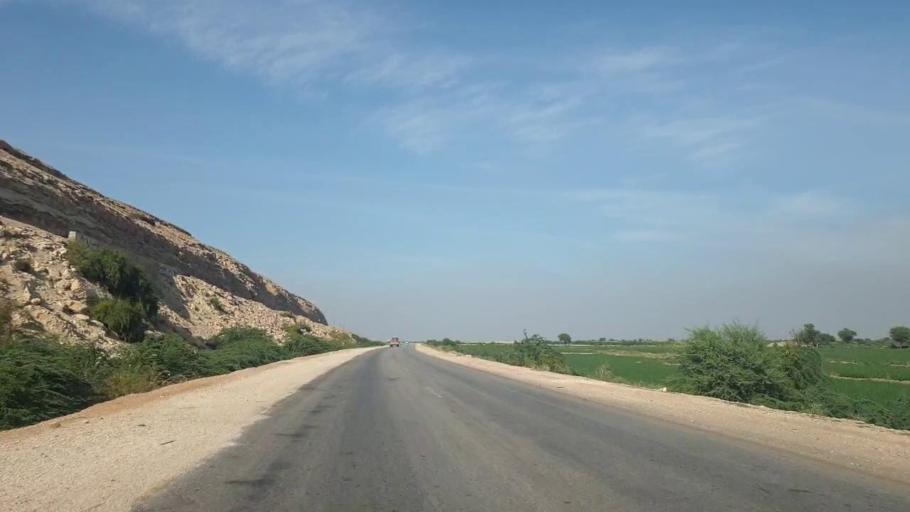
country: PK
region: Sindh
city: Sehwan
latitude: 26.3583
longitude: 67.8732
